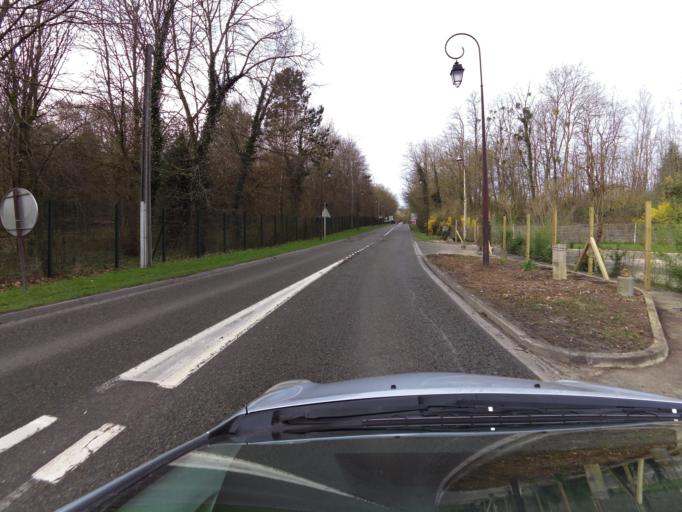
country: FR
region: Picardie
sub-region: Departement de l'Oise
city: Ver-sur-Launette
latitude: 49.1272
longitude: 2.6890
